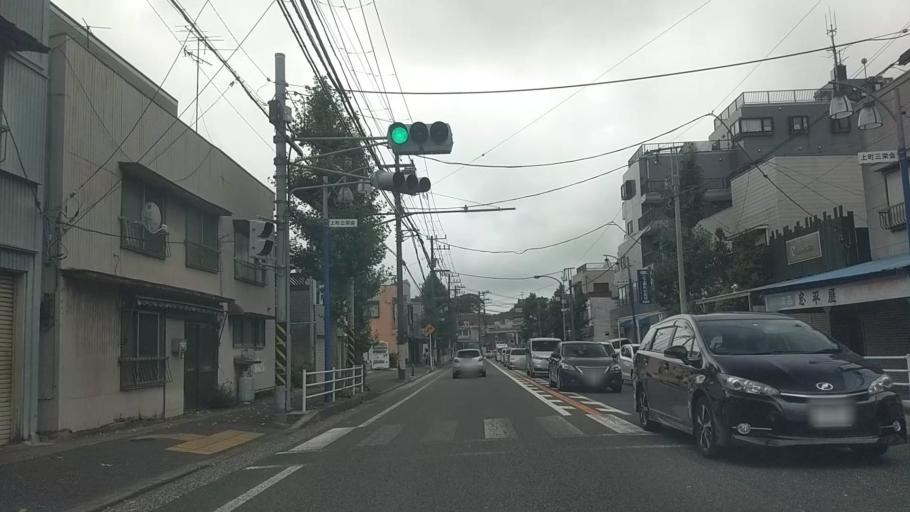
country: JP
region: Kanagawa
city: Yokosuka
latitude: 35.2707
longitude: 139.6719
